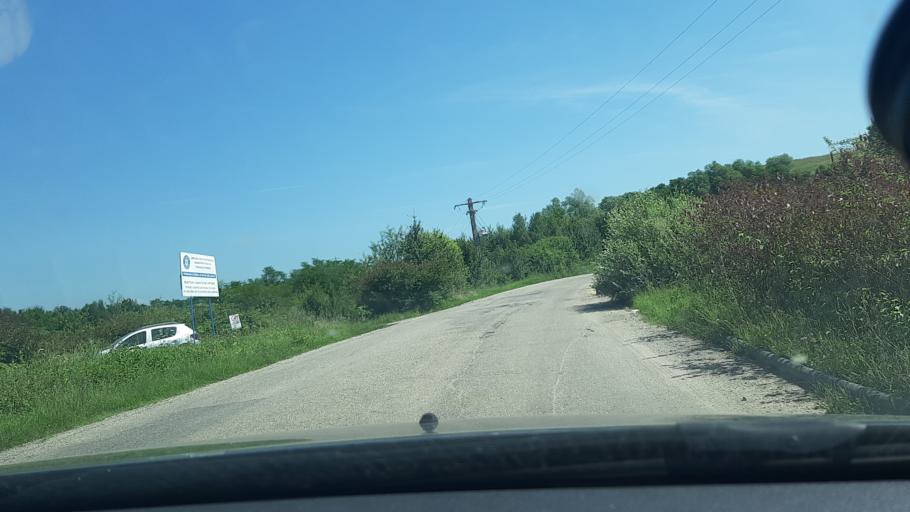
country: RO
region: Hunedoara
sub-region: Comuna Teliucu Inferior
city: Teliucu Inferior
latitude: 45.6931
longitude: 22.8732
